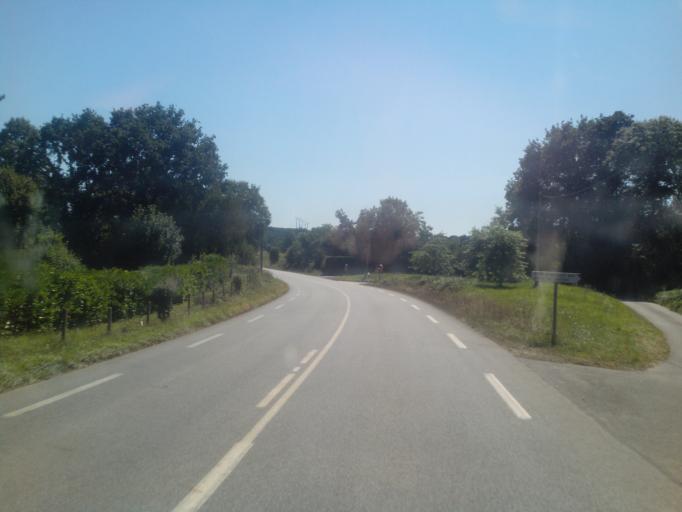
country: FR
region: Brittany
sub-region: Departement du Morbihan
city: Josselin
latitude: 47.9410
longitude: -2.5425
